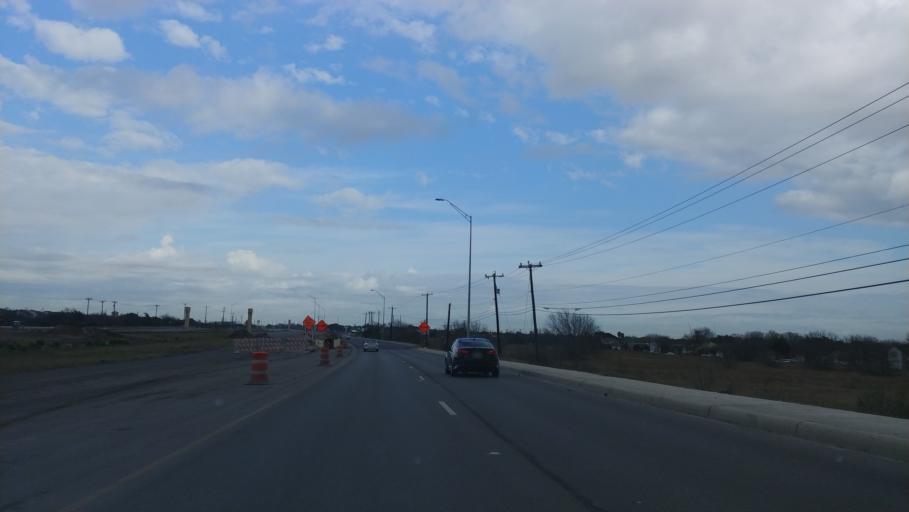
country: US
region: Texas
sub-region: Bexar County
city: Lackland Air Force Base
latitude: 29.3895
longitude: -98.7013
